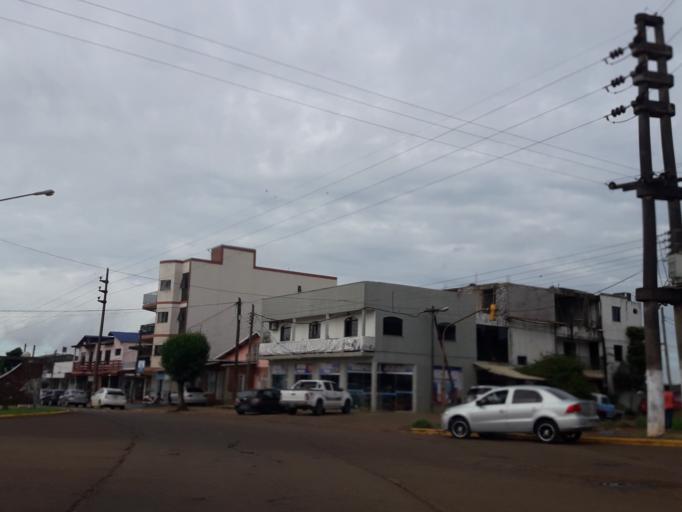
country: AR
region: Misiones
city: Bernardo de Irigoyen
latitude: -26.2568
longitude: -53.6474
